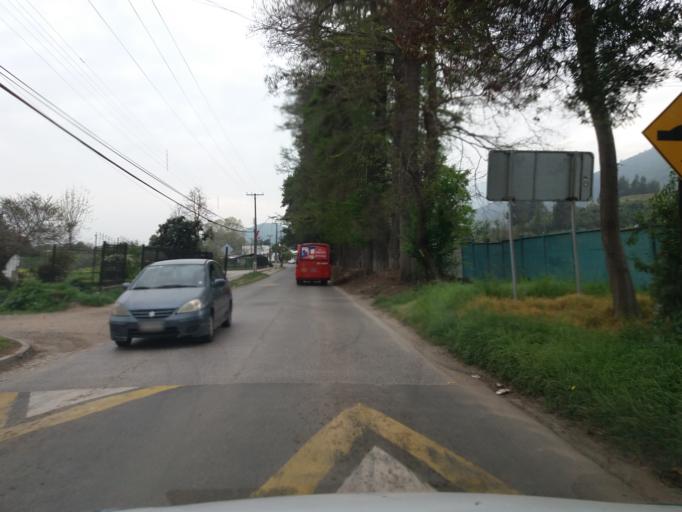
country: CL
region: Valparaiso
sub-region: Provincia de Quillota
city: Hacienda La Calera
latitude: -32.8048
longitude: -71.1430
